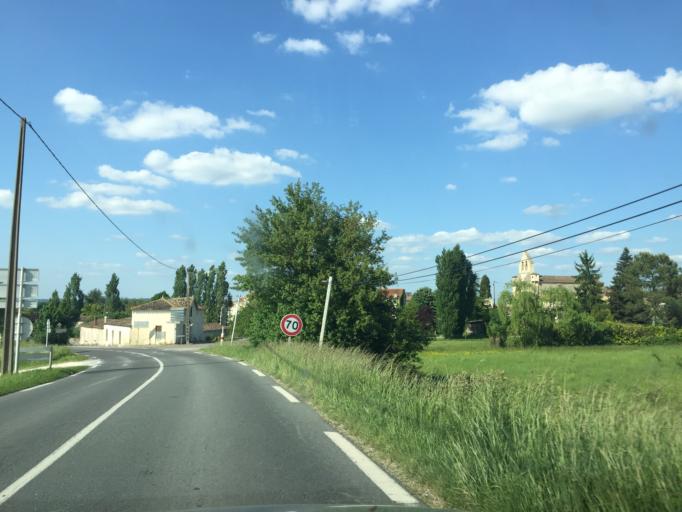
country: FR
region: Aquitaine
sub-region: Departement de la Gironde
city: Sainte-Terre
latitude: 44.8111
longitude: -0.1418
